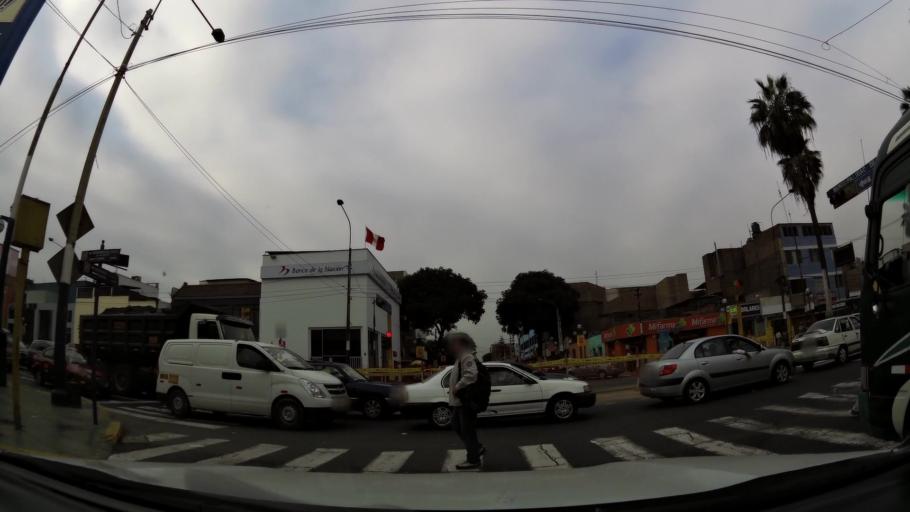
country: PE
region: Lima
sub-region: Lima
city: Surco
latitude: -12.1680
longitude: -77.0255
